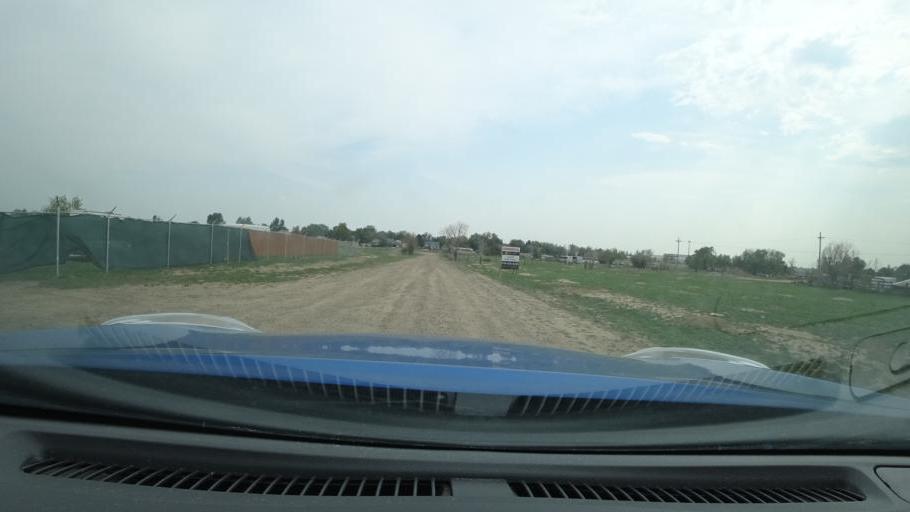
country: US
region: Colorado
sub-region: Adams County
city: Aurora
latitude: 39.7528
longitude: -104.7691
